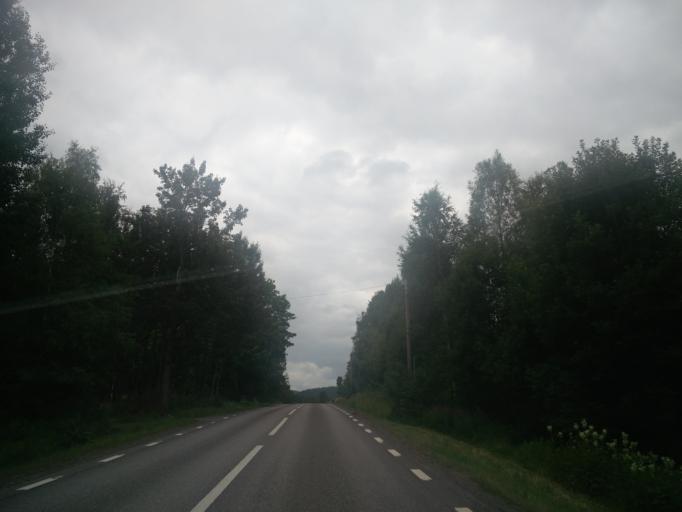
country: SE
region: Vaermland
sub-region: Torsby Kommun
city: Torsby
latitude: 59.9346
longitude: 12.9002
